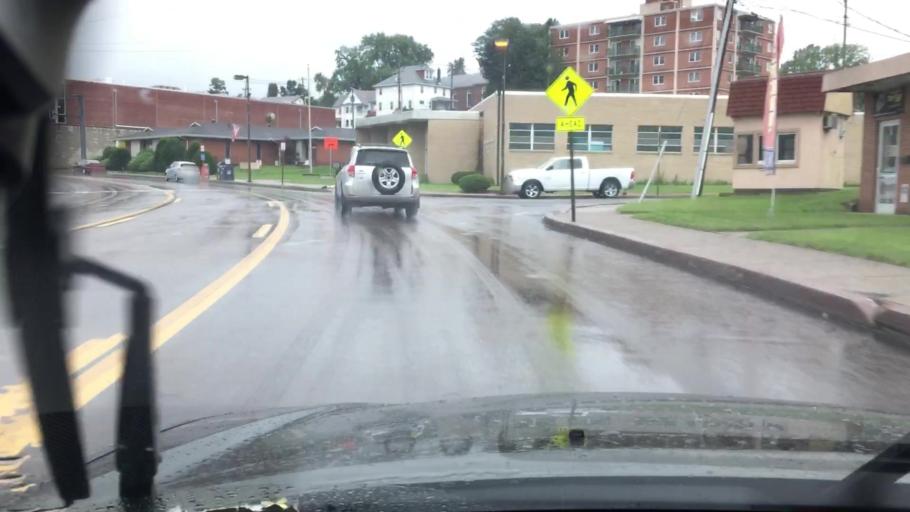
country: US
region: Pennsylvania
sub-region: Luzerne County
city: Nanticoke
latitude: 41.2064
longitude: -76.0054
